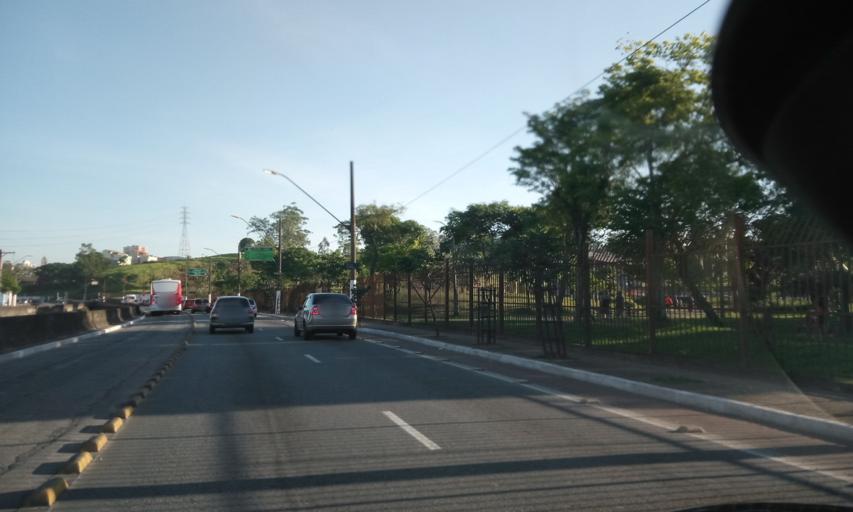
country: BR
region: Sao Paulo
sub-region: Santo Andre
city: Santo Andre
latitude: -23.6828
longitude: -46.5055
